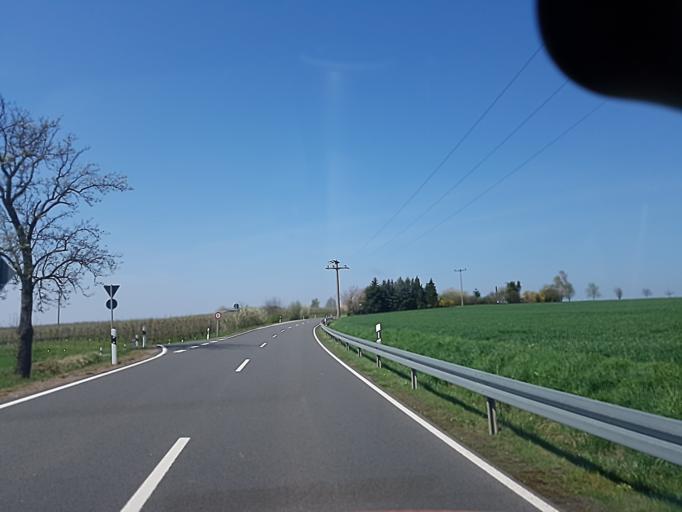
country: DE
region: Saxony
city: Ostrau
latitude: 51.2140
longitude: 12.8779
